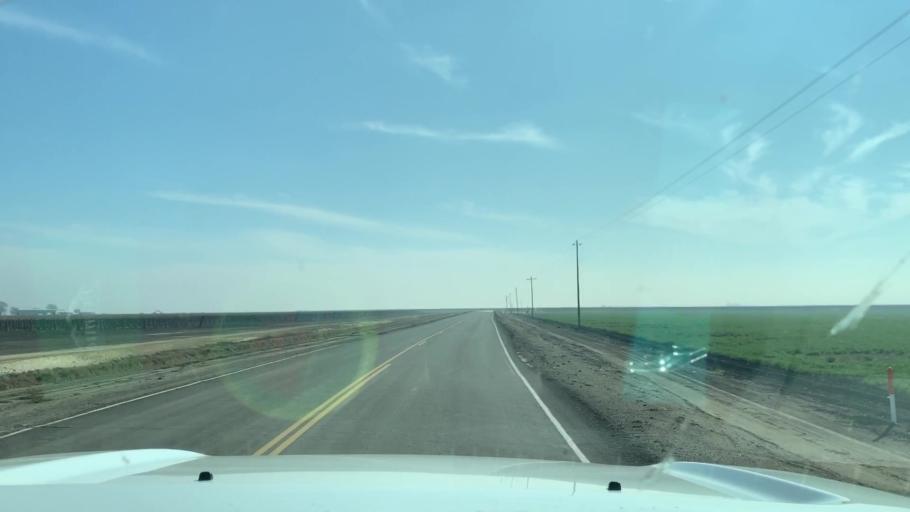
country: US
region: California
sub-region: Kern County
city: Buttonwillow
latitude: 35.4592
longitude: -119.5778
